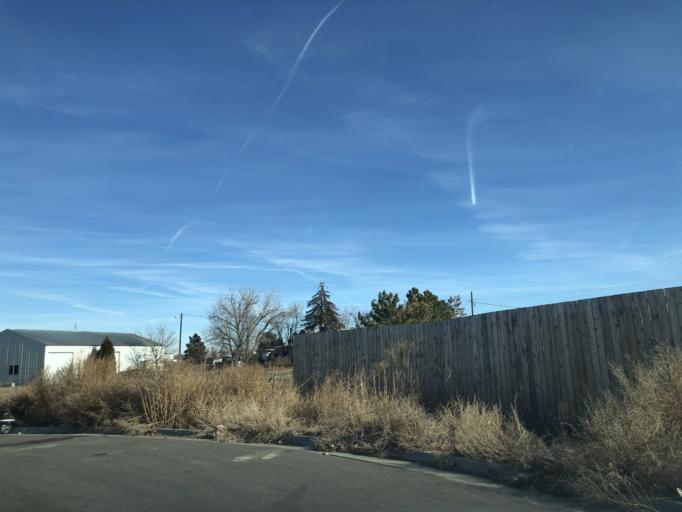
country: US
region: Colorado
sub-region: Adams County
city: Aurora
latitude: 39.7193
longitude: -104.8007
